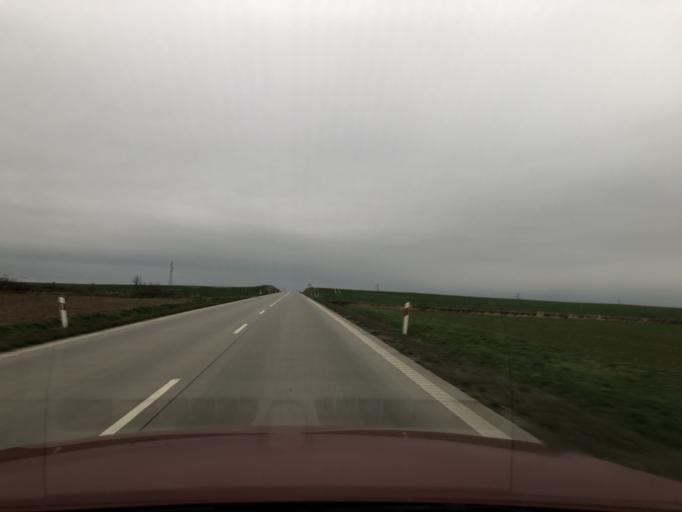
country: PL
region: Lower Silesian Voivodeship
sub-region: Powiat swidnicki
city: Zarow
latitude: 50.8979
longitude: 16.4790
